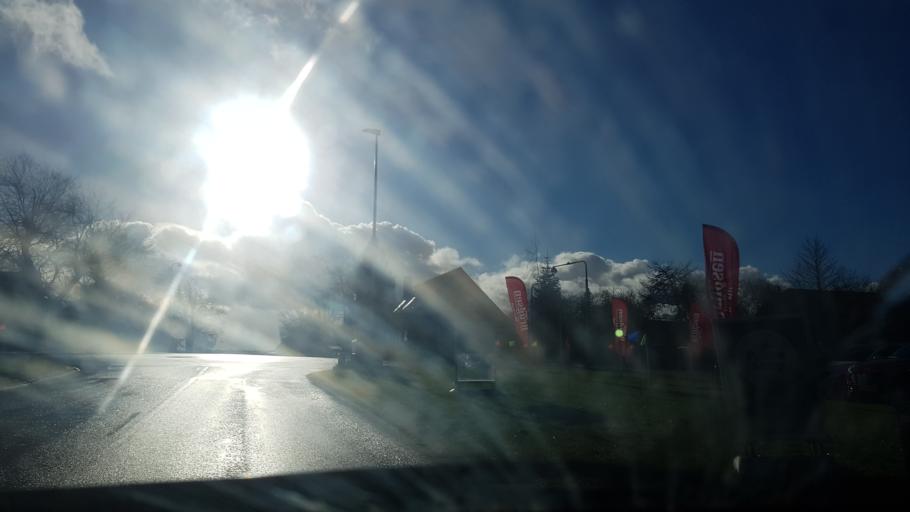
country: DK
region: South Denmark
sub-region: Fredericia Kommune
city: Taulov
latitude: 55.5192
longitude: 9.6350
